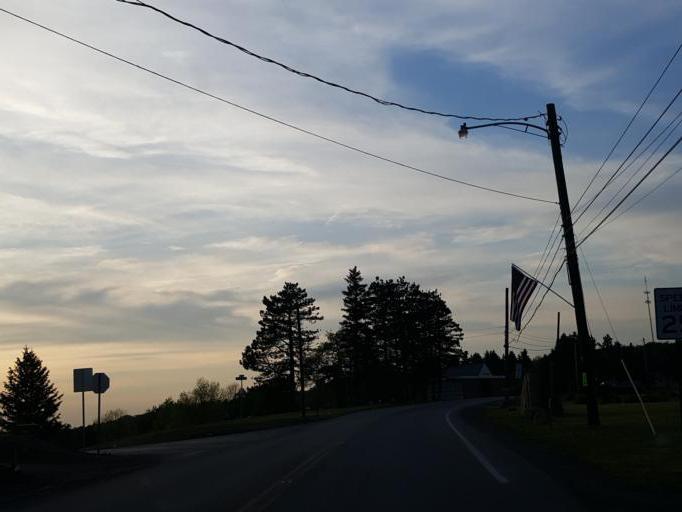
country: US
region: Pennsylvania
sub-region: Cambria County
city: Gallitzin
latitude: 40.4821
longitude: -78.5438
